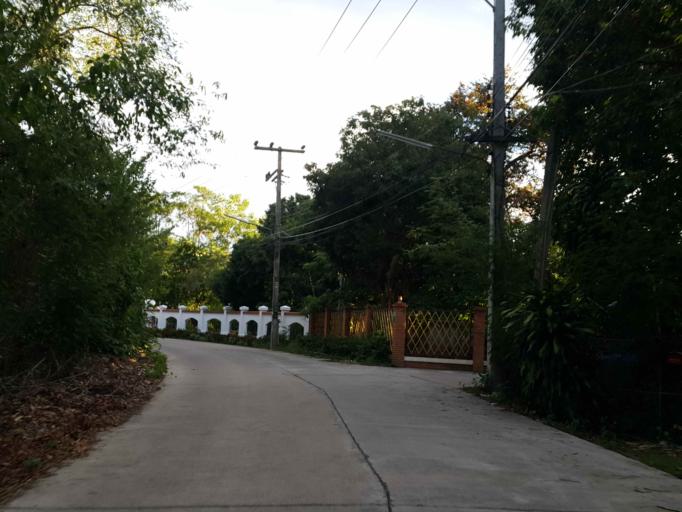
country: TH
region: Chiang Mai
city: San Sai
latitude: 18.8138
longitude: 99.0200
